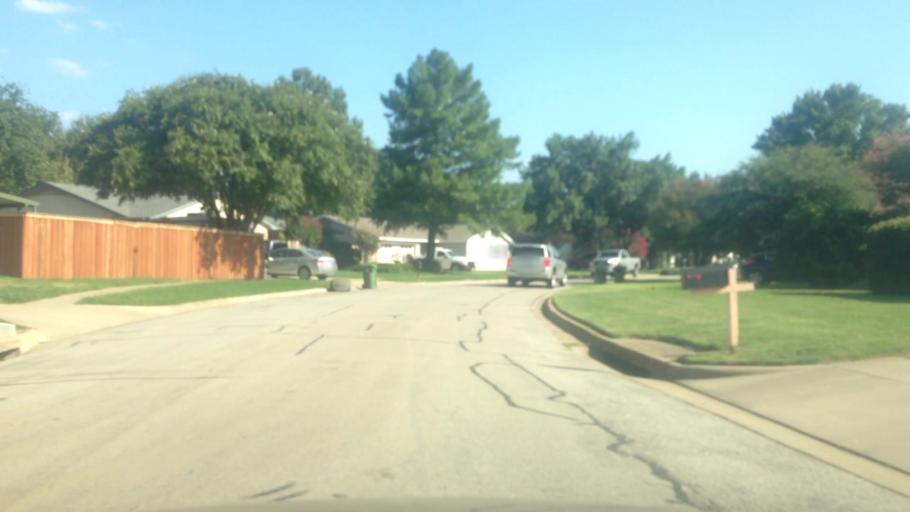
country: US
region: Texas
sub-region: Tarrant County
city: Colleyville
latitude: 32.8687
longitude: -97.1984
